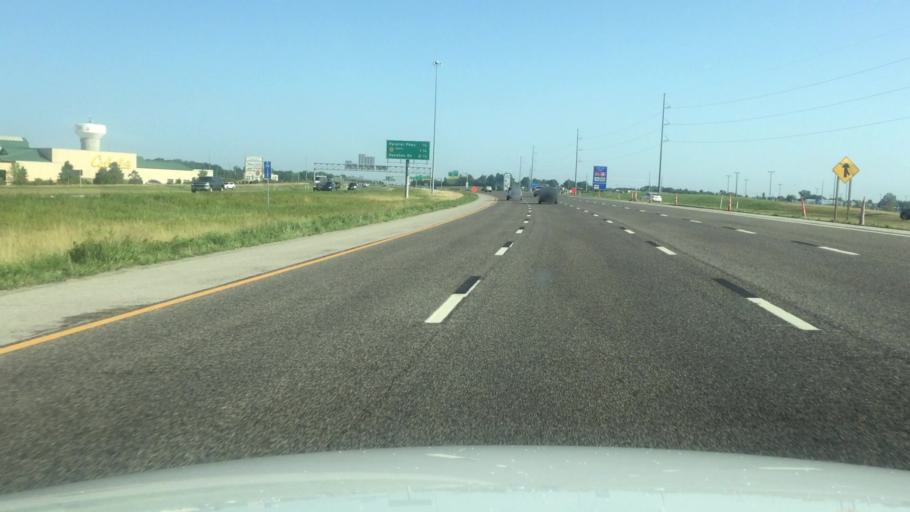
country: US
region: Kansas
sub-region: Wyandotte County
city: Edwardsville
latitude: 39.1185
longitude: -94.8120
